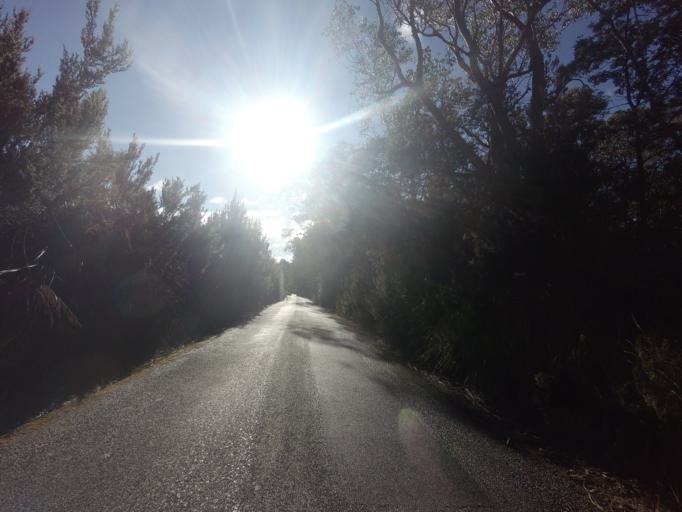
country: AU
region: Tasmania
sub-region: Glenorchy
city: Berriedale
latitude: -42.8406
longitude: 147.1581
